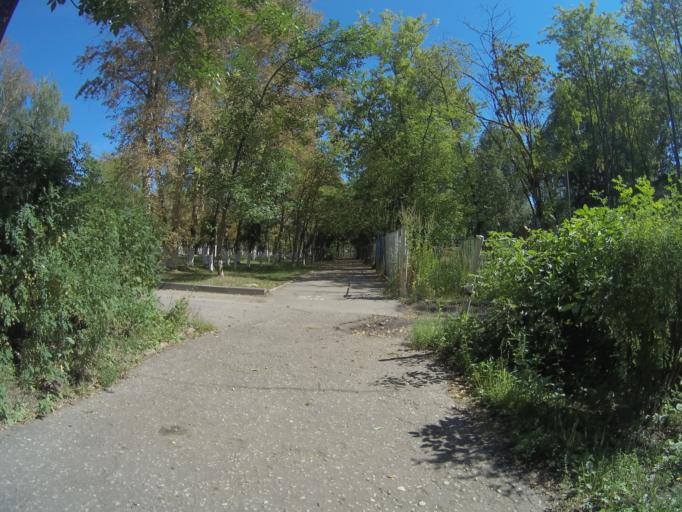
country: RU
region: Vladimir
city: Vladimir
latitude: 56.1309
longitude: 40.3633
